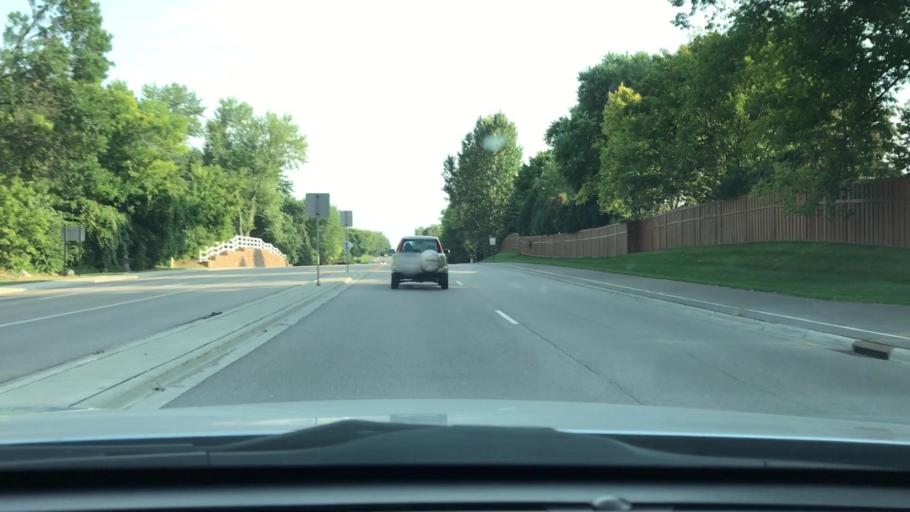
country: US
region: Minnesota
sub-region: Hennepin County
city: Maple Grove
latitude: 45.0432
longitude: -93.4818
